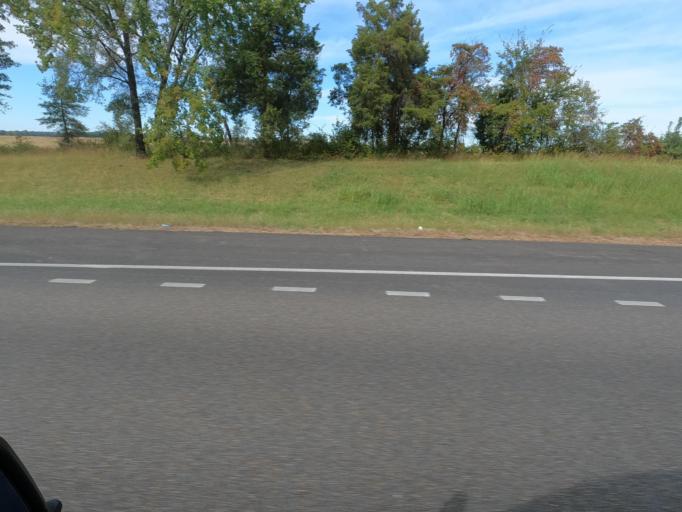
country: US
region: Tennessee
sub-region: Tipton County
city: Mason
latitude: 35.3899
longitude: -89.4160
